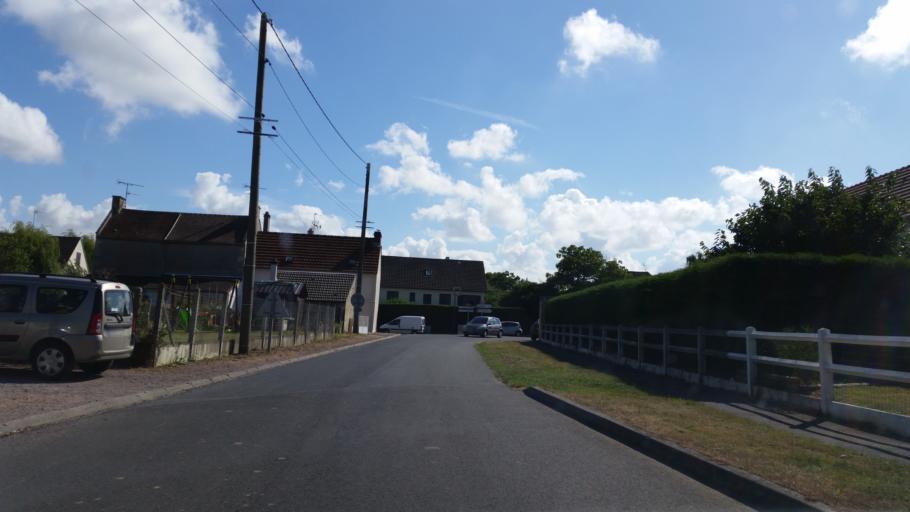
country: FR
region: Lower Normandy
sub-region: Departement du Calvados
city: Amfreville
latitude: 49.2508
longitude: -0.2317
